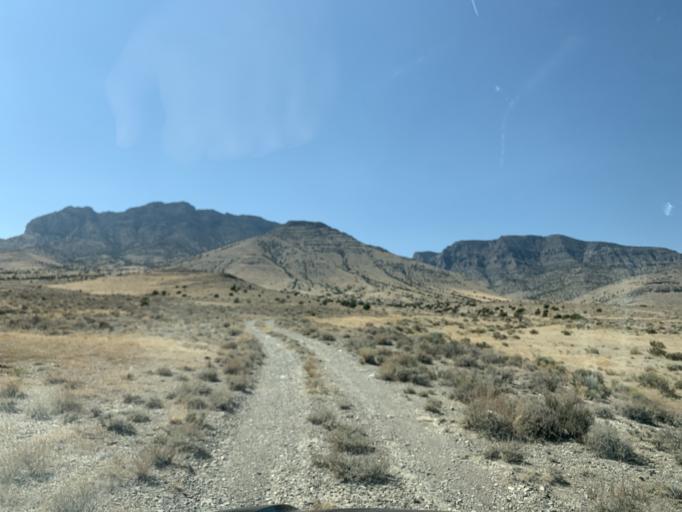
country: US
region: Utah
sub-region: Beaver County
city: Milford
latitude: 38.9764
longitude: -113.4593
